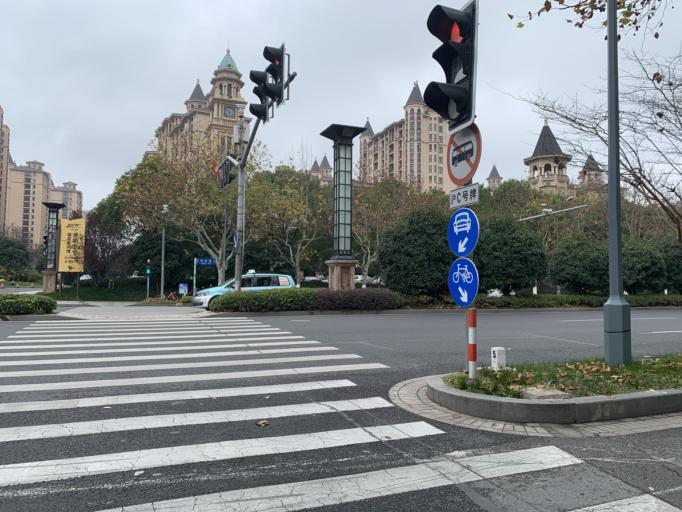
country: CN
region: Shanghai Shi
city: Huamu
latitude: 31.1949
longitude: 121.5349
